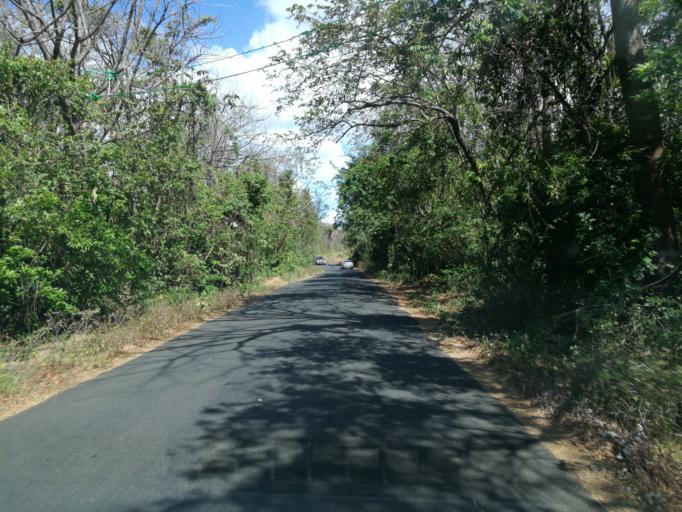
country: CR
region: Guanacaste
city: Liberia
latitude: 10.7510
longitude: -85.3715
